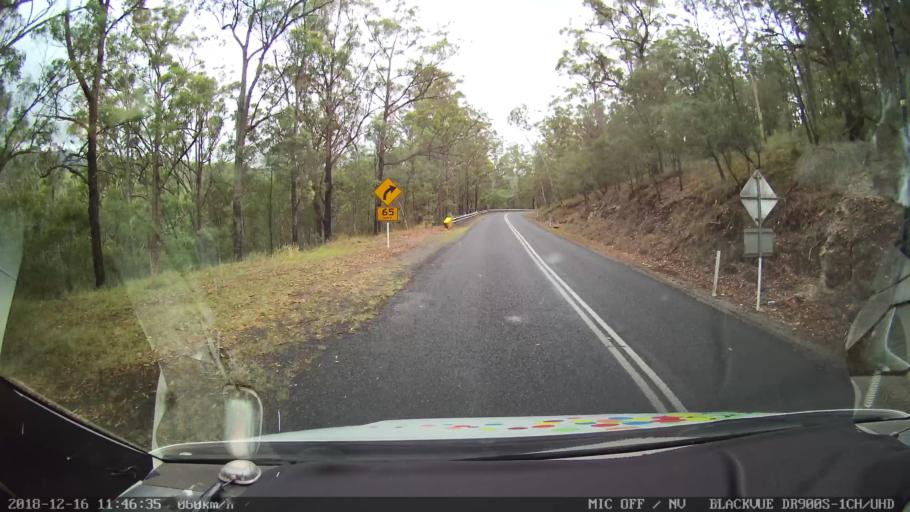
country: AU
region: New South Wales
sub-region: Tenterfield Municipality
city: Carrolls Creek
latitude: -28.9270
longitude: 152.2315
